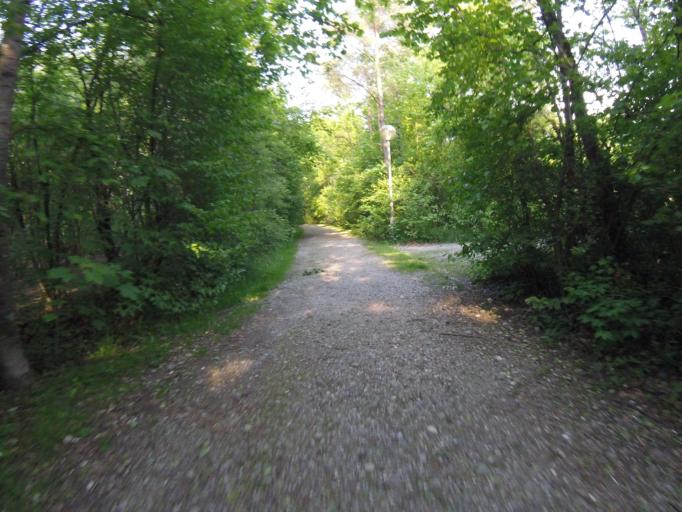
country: DE
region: Bavaria
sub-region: Upper Bavaria
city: Ottobrunn
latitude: 48.0542
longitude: 11.6595
